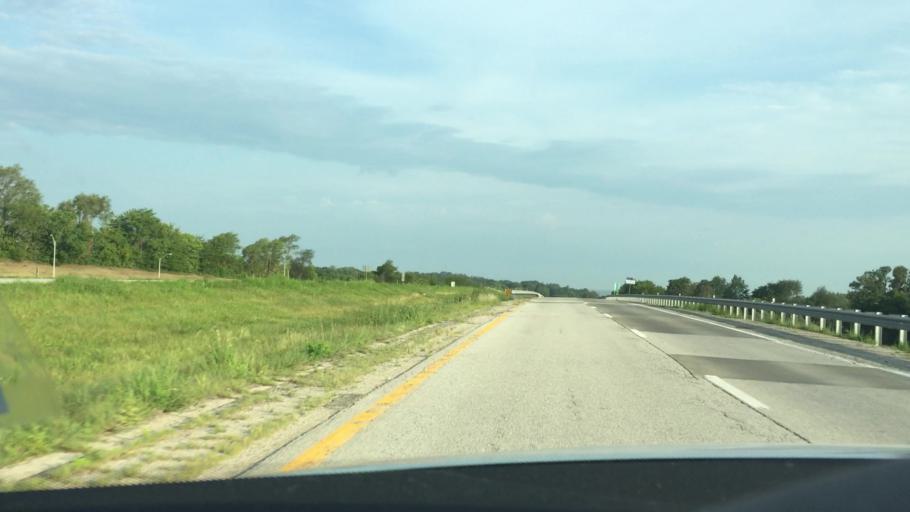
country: US
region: Missouri
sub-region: Buchanan County
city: Saint Joseph
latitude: 39.7209
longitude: -94.8321
